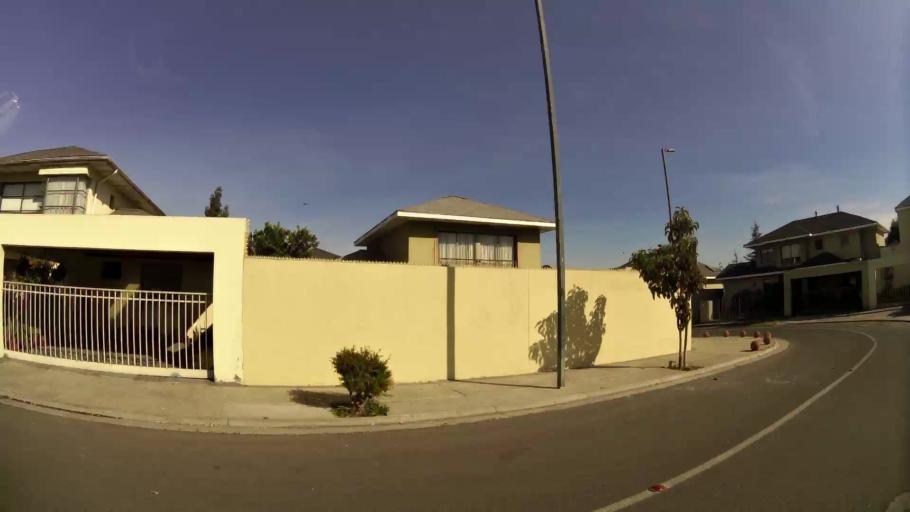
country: CL
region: Santiago Metropolitan
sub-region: Provincia de Santiago
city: Villa Presidente Frei, Nunoa, Santiago, Chile
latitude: -33.4918
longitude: -70.5512
